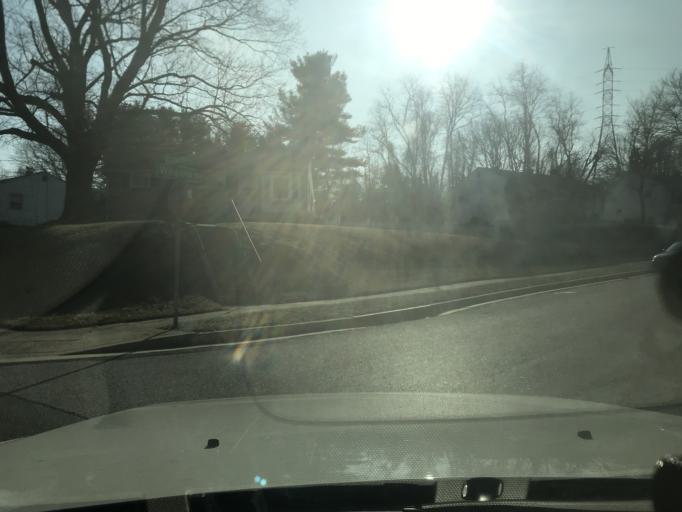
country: US
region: Maryland
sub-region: Baltimore County
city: Owings Mills
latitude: 39.4198
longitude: -76.7905
